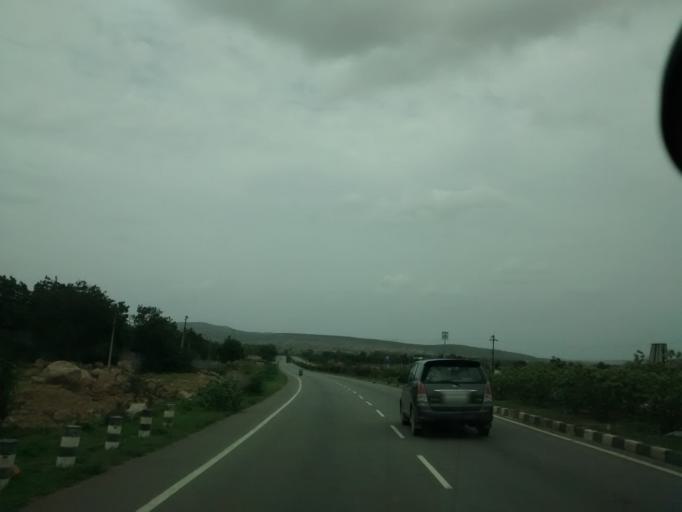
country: IN
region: Andhra Pradesh
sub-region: Kurnool
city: Ramapuram
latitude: 15.2540
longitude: 77.7522
